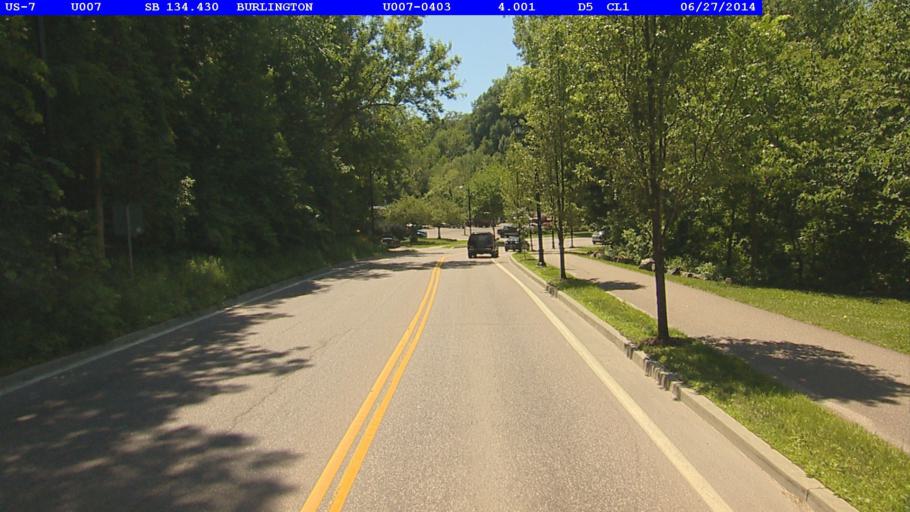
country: US
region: Vermont
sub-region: Chittenden County
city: Winooski
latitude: 44.4866
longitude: -73.1881
